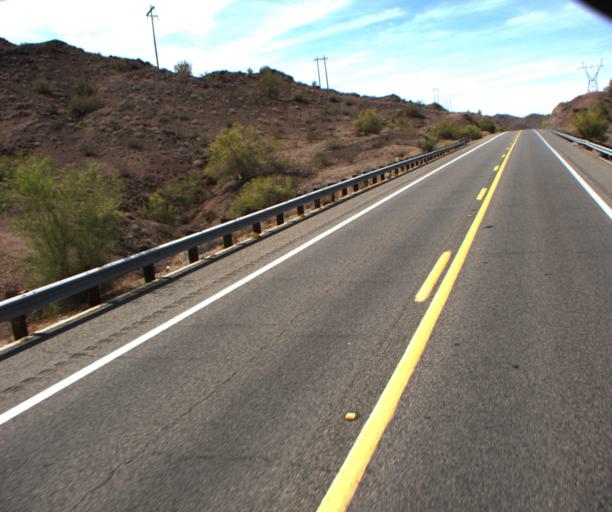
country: US
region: Arizona
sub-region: La Paz County
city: Cienega Springs
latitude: 34.3467
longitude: -114.1501
